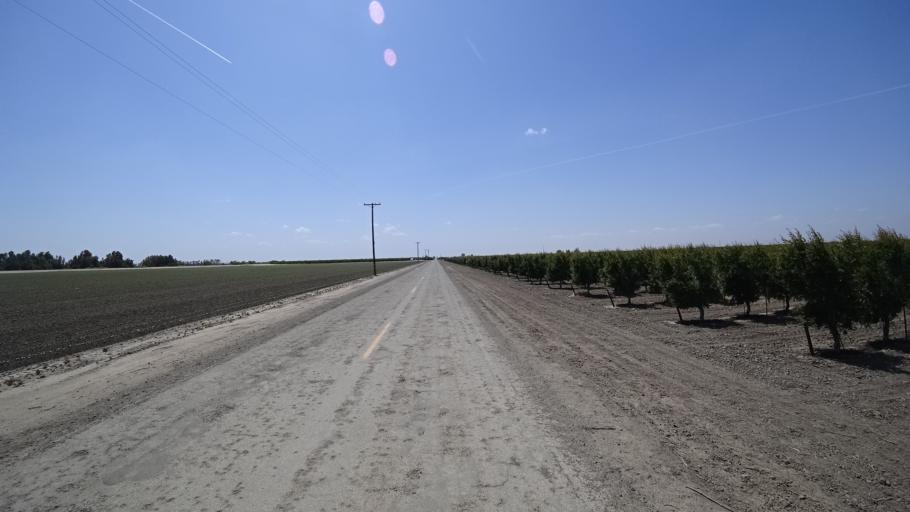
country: US
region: California
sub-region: Kings County
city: Stratford
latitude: 36.2008
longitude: -119.8515
